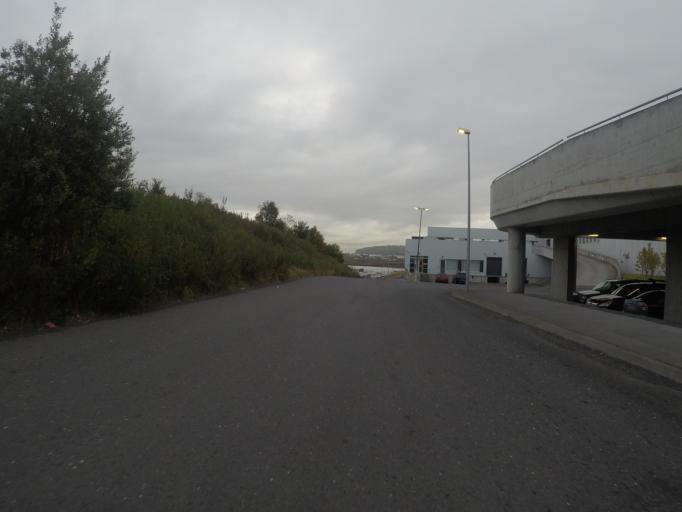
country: IS
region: Capital Region
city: Reykjavik
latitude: 64.1430
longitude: -21.8489
